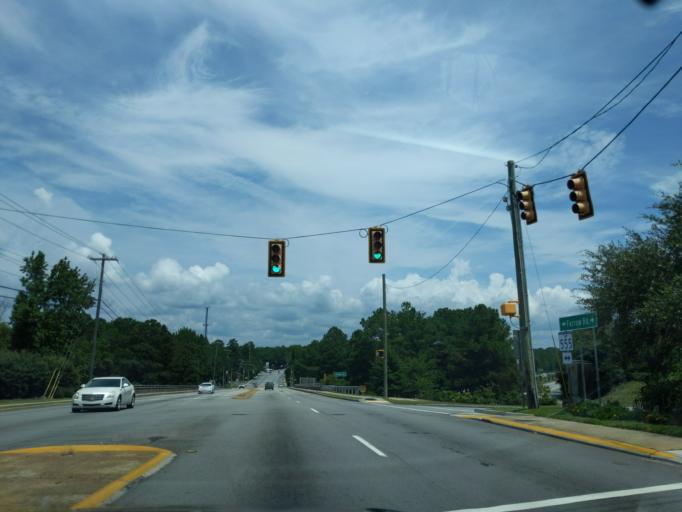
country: US
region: South Carolina
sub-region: Richland County
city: Columbia
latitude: 34.0344
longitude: -81.0232
